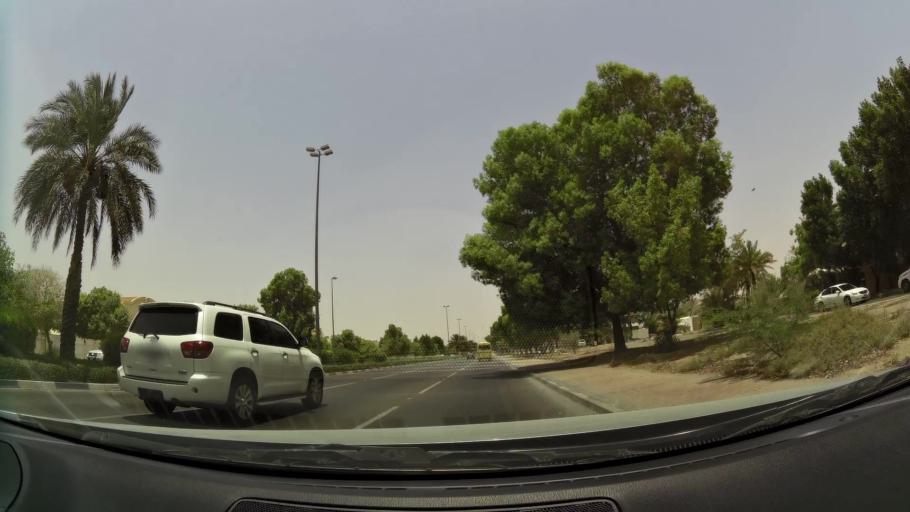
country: AE
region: Abu Dhabi
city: Al Ain
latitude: 24.2058
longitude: 55.7427
